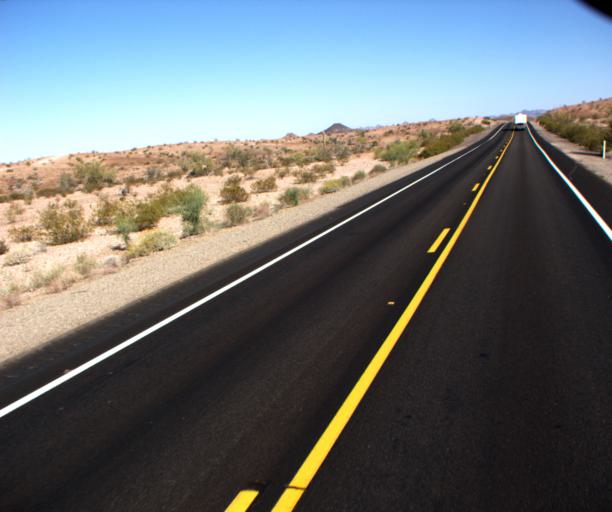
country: US
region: Arizona
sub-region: Yuma County
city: Wellton
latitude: 33.0795
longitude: -114.2955
